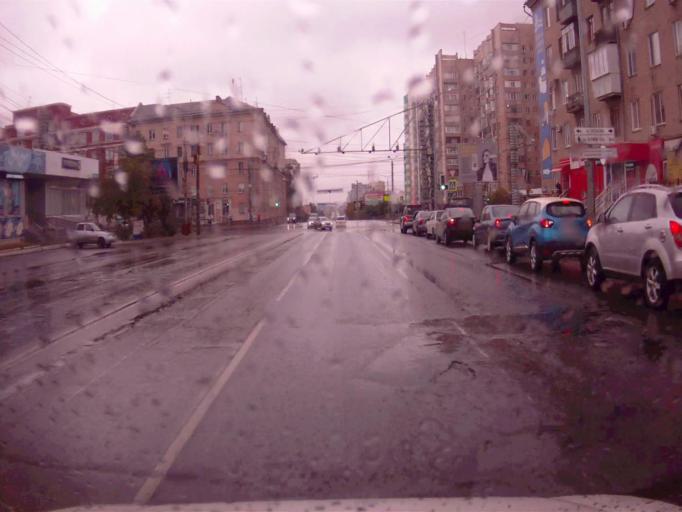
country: RU
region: Chelyabinsk
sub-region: Gorod Chelyabinsk
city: Chelyabinsk
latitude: 55.1599
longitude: 61.4166
